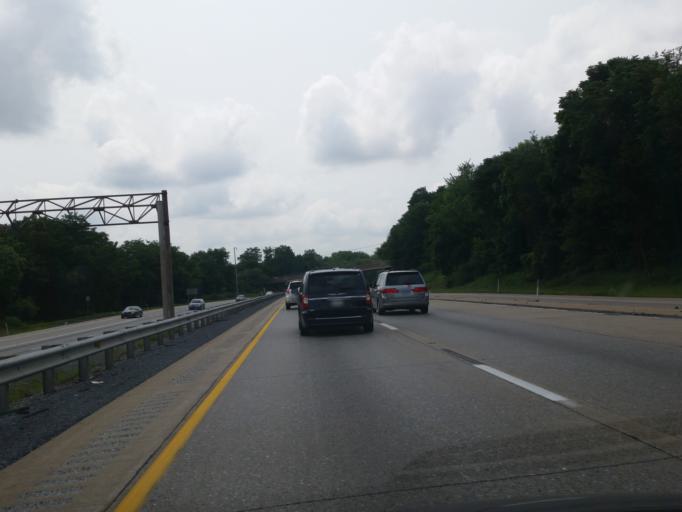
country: US
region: Pennsylvania
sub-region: Dauphin County
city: Paxtonia
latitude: 40.3255
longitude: -76.7944
